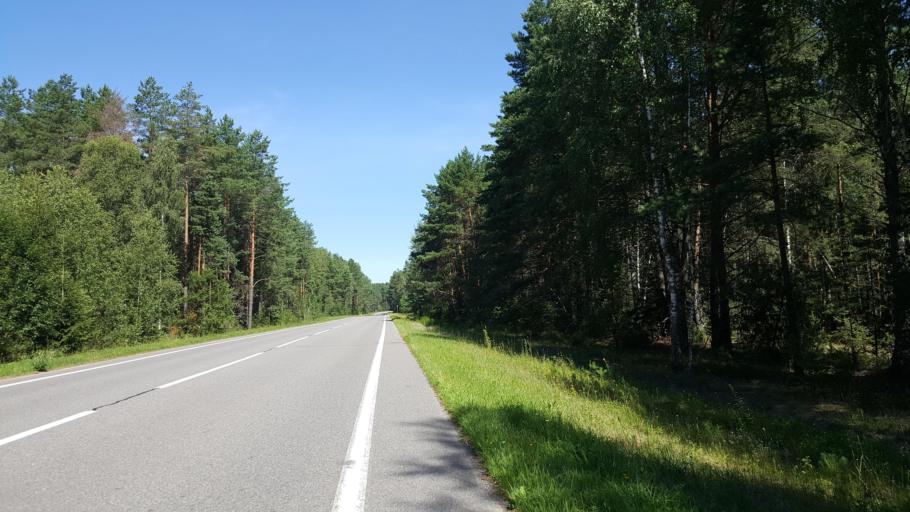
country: BY
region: Brest
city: Pruzhany
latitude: 52.4900
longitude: 24.1712
